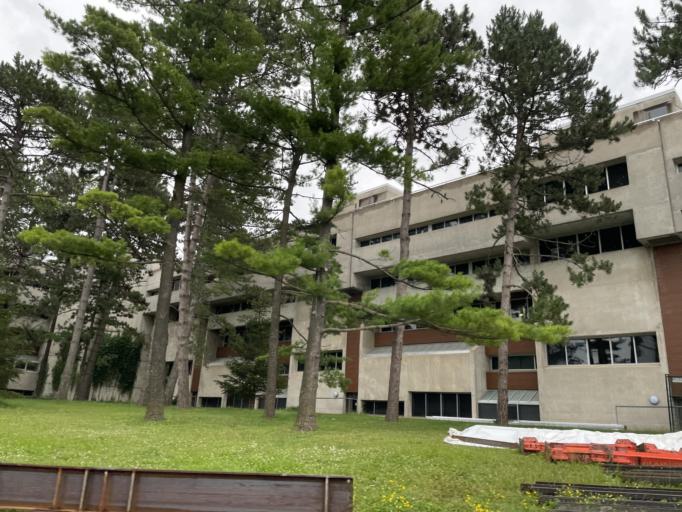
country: CA
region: Ontario
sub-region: Wellington County
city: Guelph
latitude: 43.5306
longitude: -80.2225
